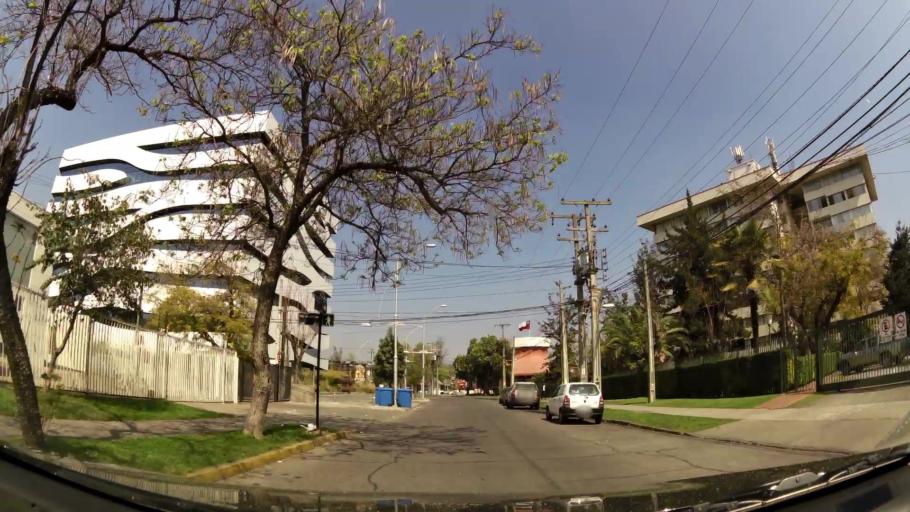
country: CL
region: Santiago Metropolitan
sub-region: Provincia de Santiago
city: Villa Presidente Frei, Nunoa, Santiago, Chile
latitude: -33.3870
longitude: -70.5668
